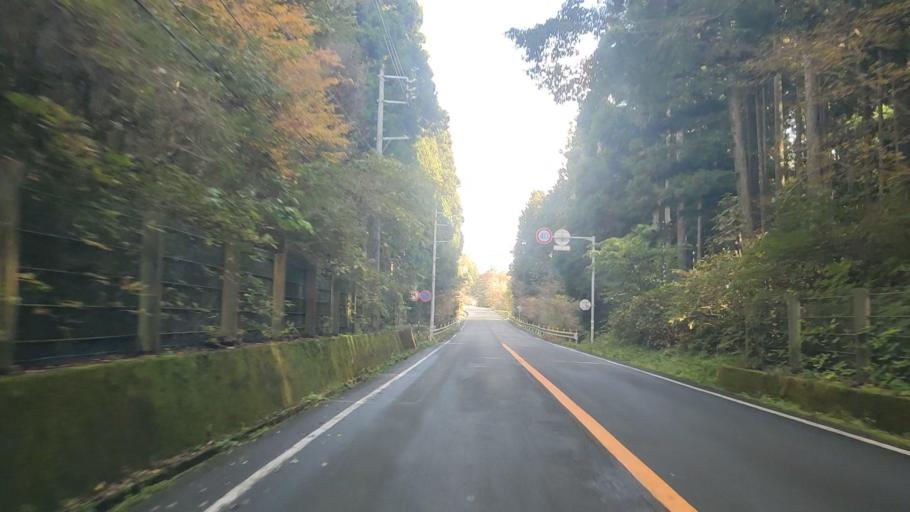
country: JP
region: Shizuoka
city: Fujinomiya
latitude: 35.2961
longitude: 138.6662
